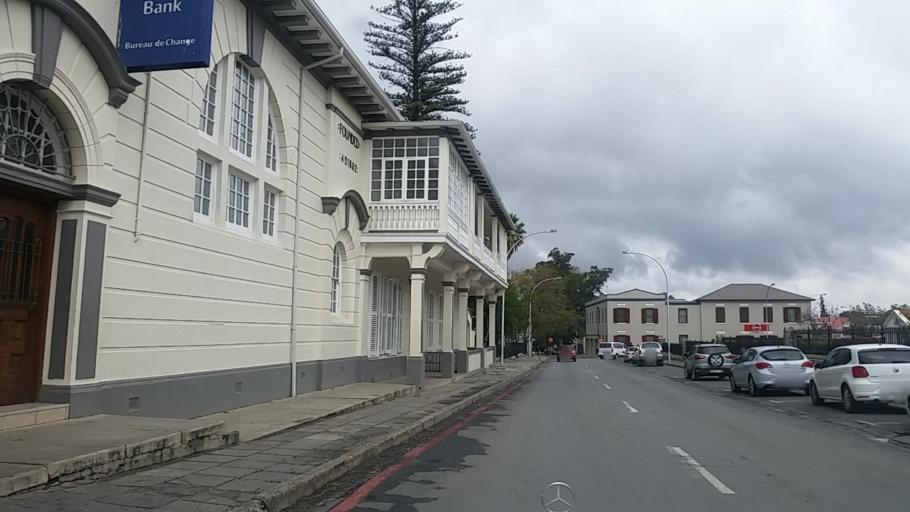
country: ZA
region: Eastern Cape
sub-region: Cacadu District Municipality
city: Graaff-Reinet
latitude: -32.2491
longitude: 24.5353
